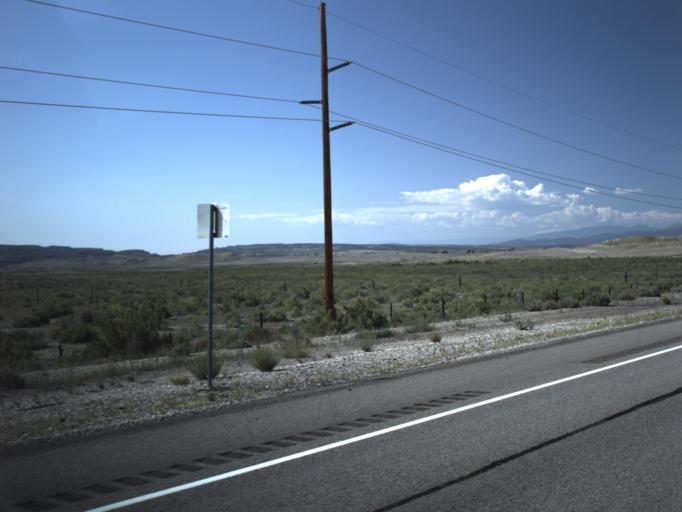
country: US
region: Utah
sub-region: Emery County
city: Ferron
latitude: 38.9476
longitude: -111.2134
